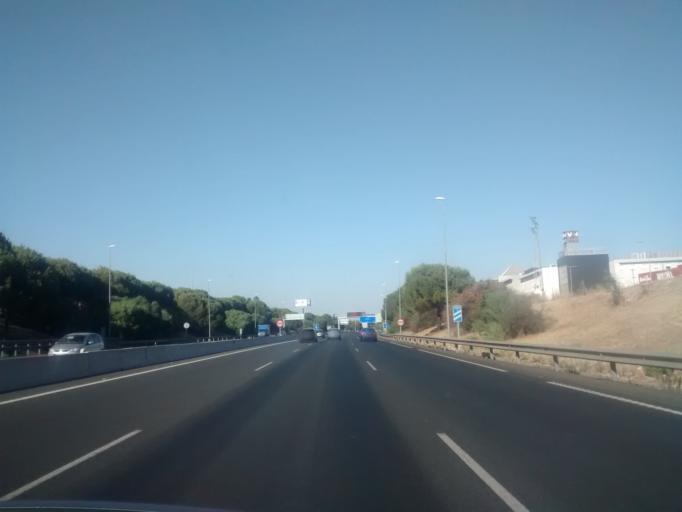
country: ES
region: Andalusia
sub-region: Provincia de Sevilla
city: Bormujos
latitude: 37.3810
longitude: -6.0715
